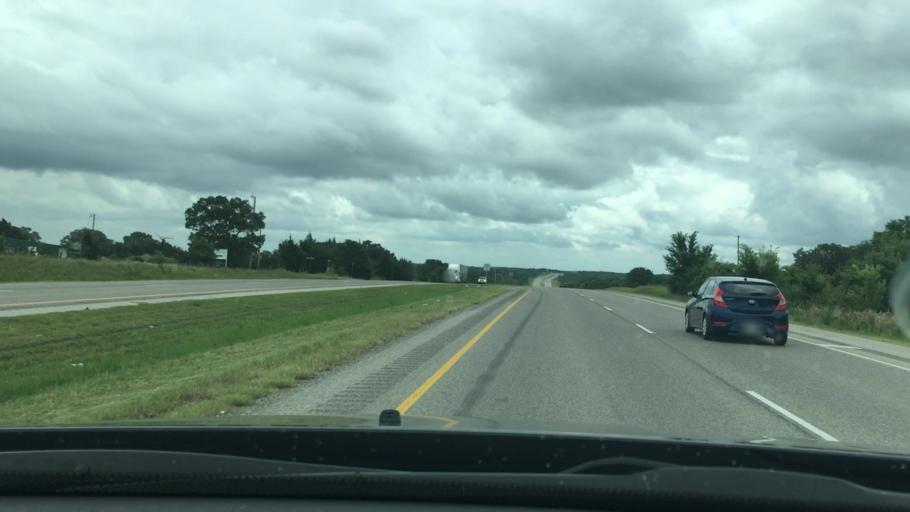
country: US
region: Oklahoma
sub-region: Carter County
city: Ardmore
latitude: 34.1276
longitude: -97.0747
